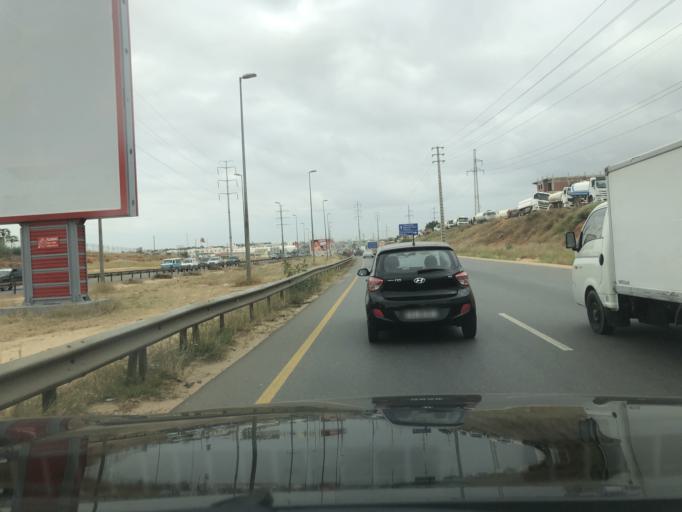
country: AO
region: Luanda
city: Luanda
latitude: -8.9743
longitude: 13.2161
